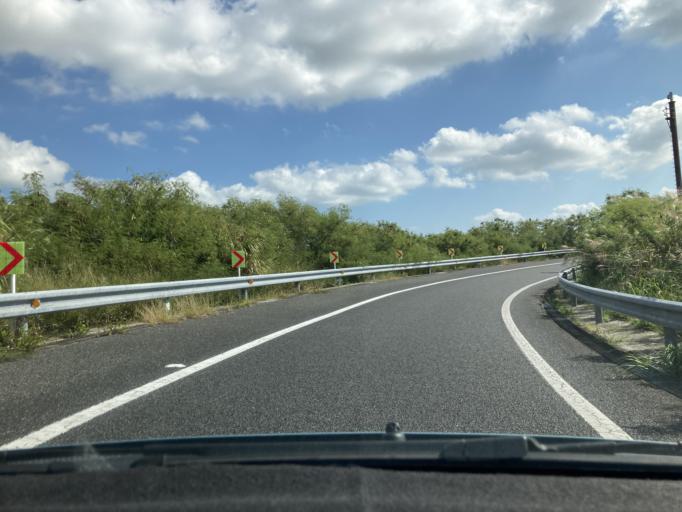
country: JP
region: Okinawa
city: Tomigusuku
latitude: 26.1728
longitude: 127.6970
